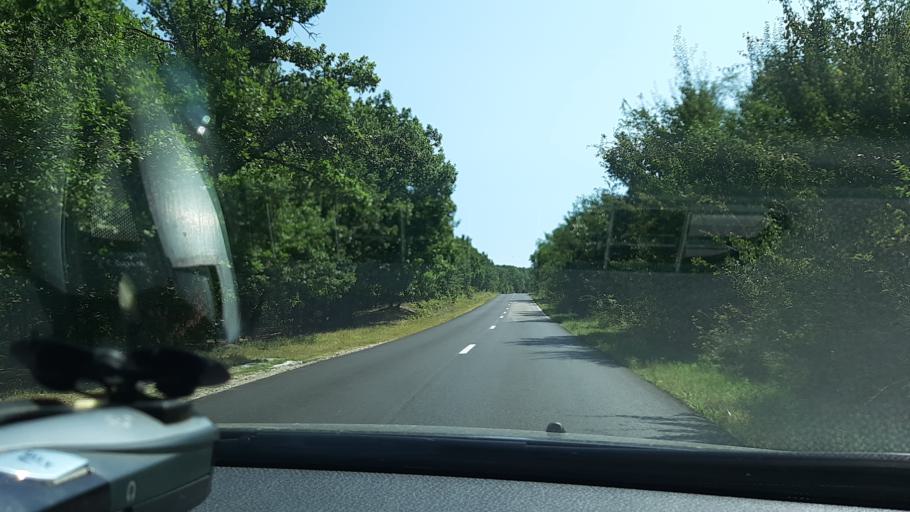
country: RO
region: Gorj
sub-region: Comuna Targu Carbunesti
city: Targu Carbunesti
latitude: 44.9480
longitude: 23.5662
